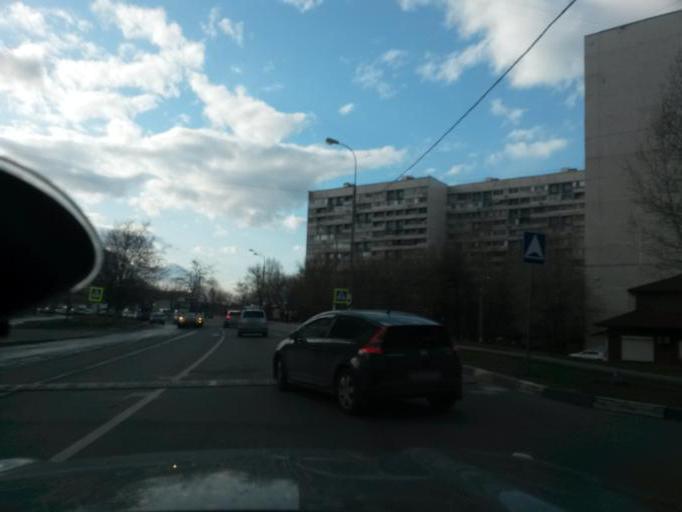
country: RU
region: Moscow
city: Orekhovo-Borisovo
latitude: 55.6254
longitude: 37.7270
